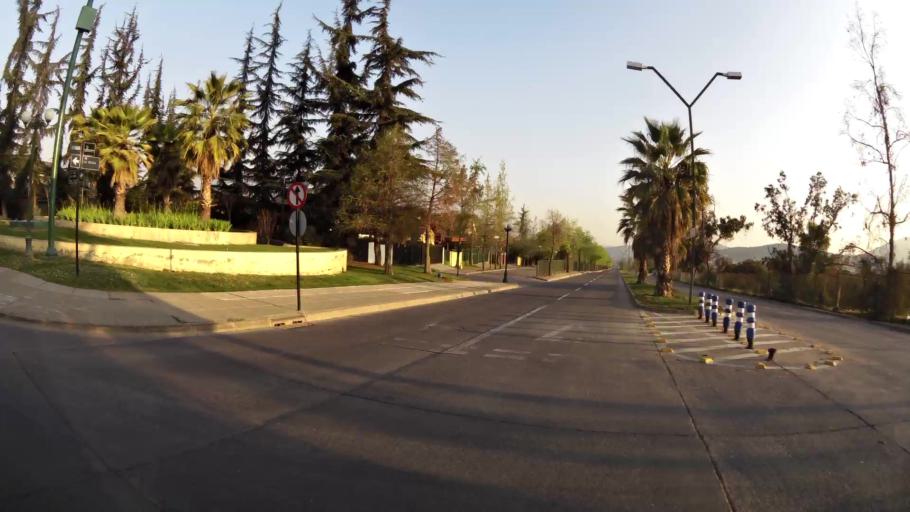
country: CL
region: Santiago Metropolitan
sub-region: Provincia de Chacabuco
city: Chicureo Abajo
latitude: -33.3268
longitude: -70.5193
